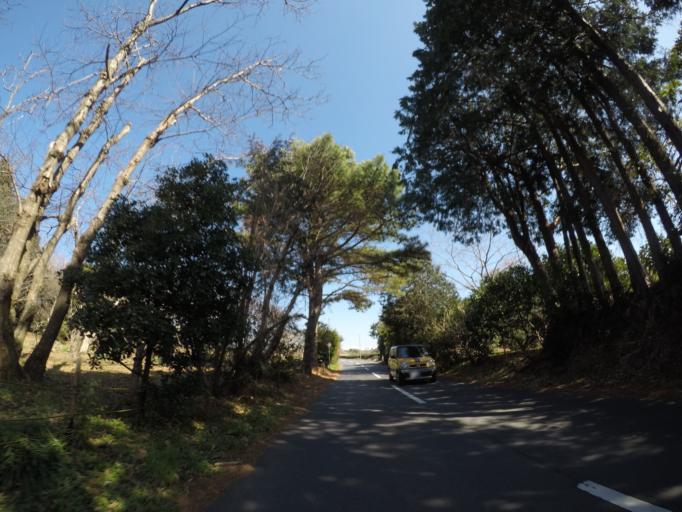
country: JP
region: Shizuoka
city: Numazu
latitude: 35.1437
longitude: 138.8222
